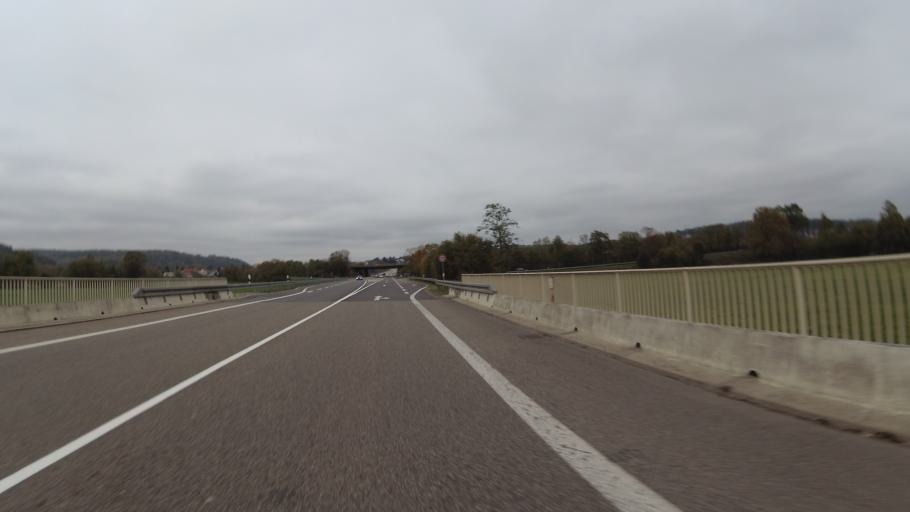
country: DE
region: Saarland
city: Blieskastel
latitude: 49.2651
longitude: 7.3096
